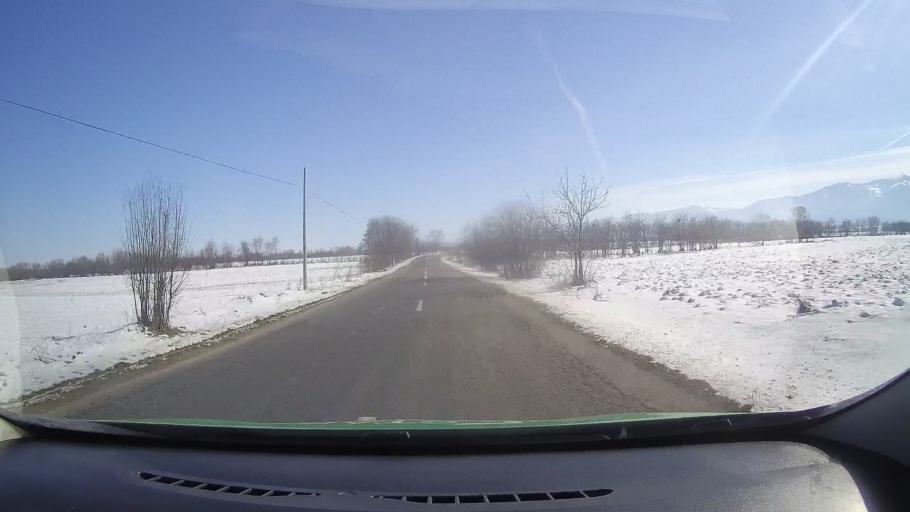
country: RO
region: Brasov
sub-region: Comuna Recea
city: Recea
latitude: 45.7315
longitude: 24.9556
